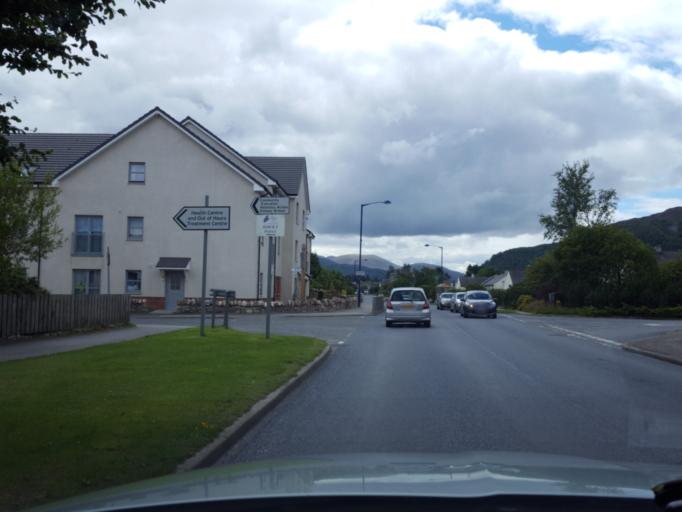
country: GB
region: Scotland
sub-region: Highland
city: Aviemore
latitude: 57.1987
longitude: -3.8287
